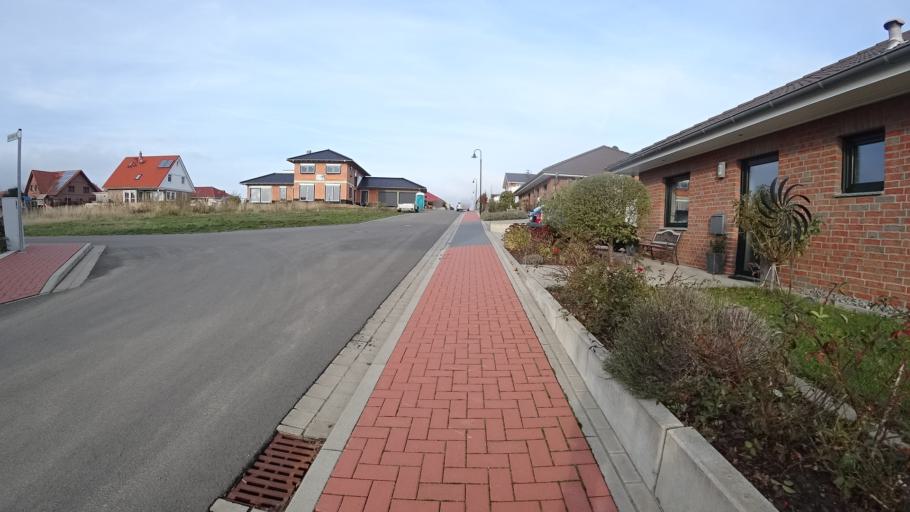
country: DE
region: Lower Saxony
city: Lauenau
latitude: 52.2784
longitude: 9.3791
